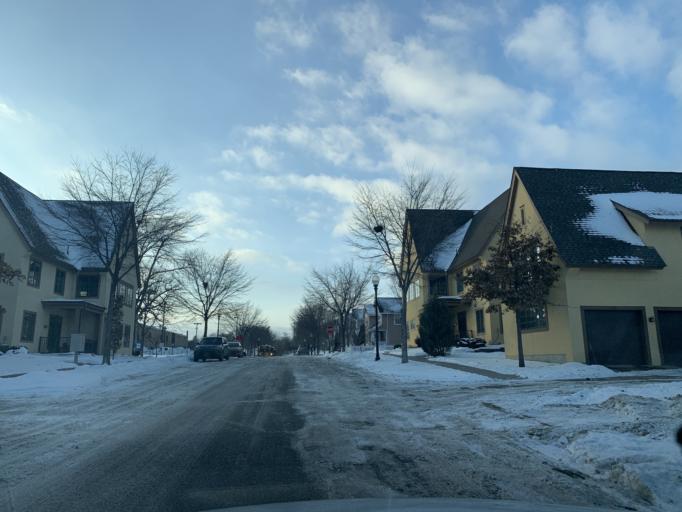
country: US
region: Minnesota
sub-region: Hennepin County
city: Minneapolis
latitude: 44.9882
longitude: -93.2933
